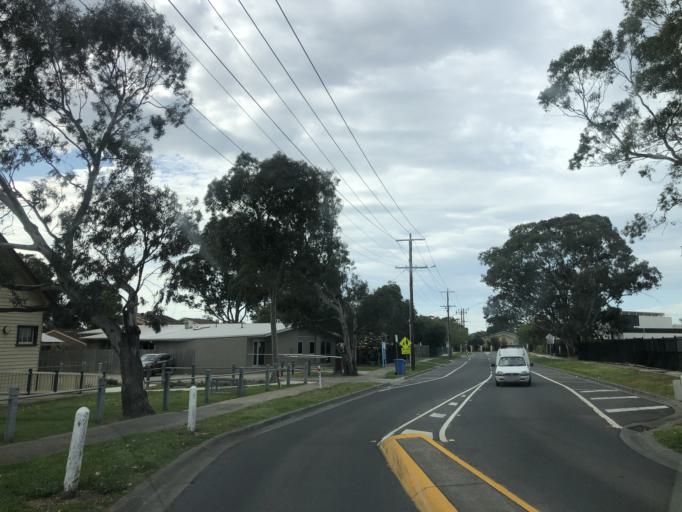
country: AU
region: Victoria
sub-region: Casey
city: Hampton Park
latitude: -38.0317
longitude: 145.2517
